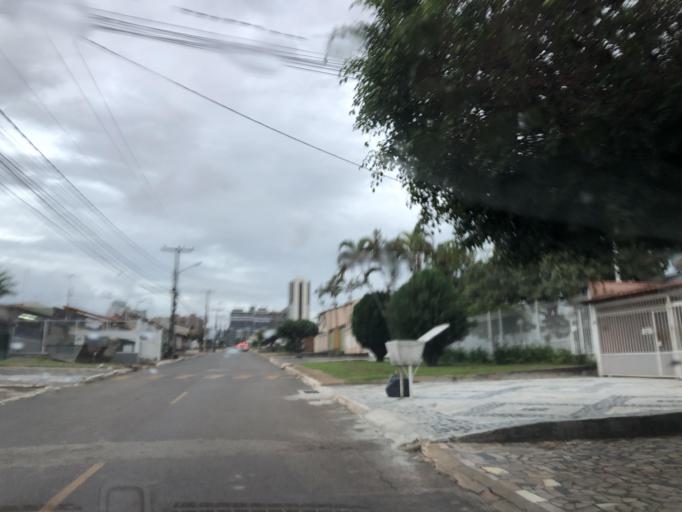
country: BR
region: Federal District
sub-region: Brasilia
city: Brasilia
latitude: -15.8401
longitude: -48.0606
